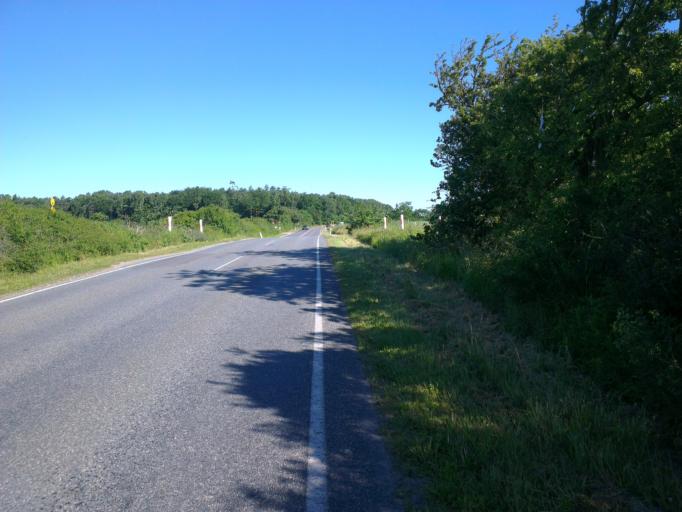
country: DK
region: Capital Region
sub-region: Frederikssund Kommune
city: Jaegerspris
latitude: 55.8737
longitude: 11.9579
